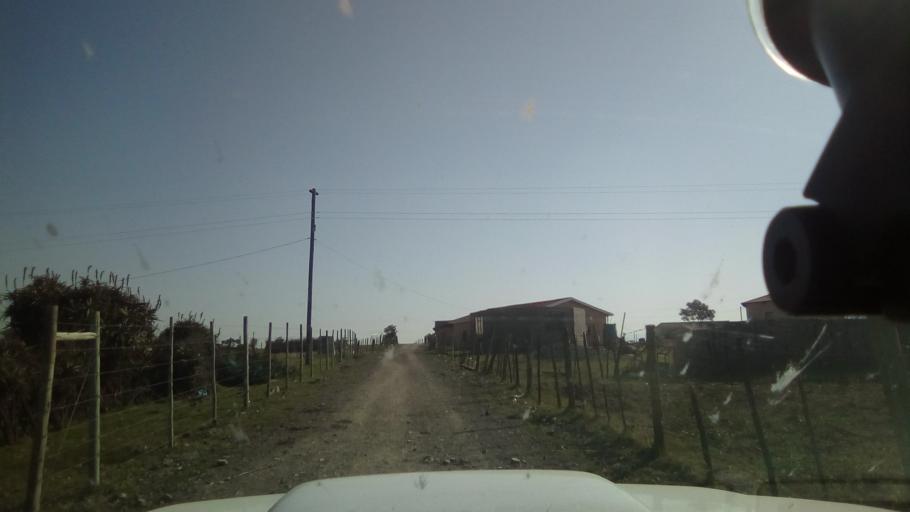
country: ZA
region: Eastern Cape
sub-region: Buffalo City Metropolitan Municipality
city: Bhisho
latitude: -32.9534
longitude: 27.3185
